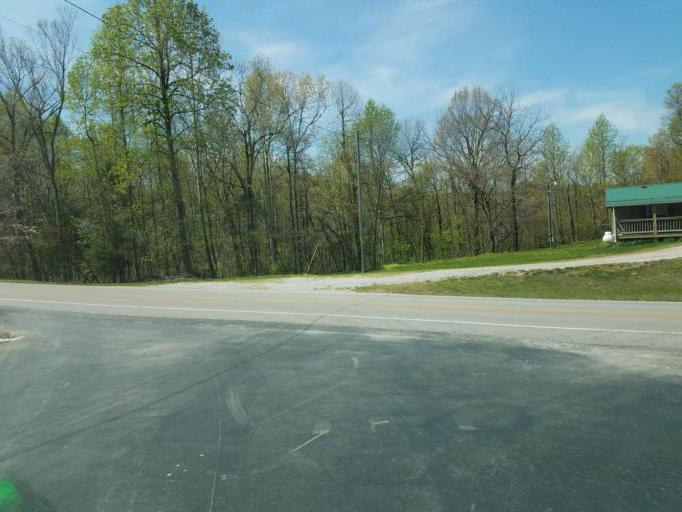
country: US
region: Kentucky
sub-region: Barren County
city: Cave City
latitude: 37.1439
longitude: -86.0378
